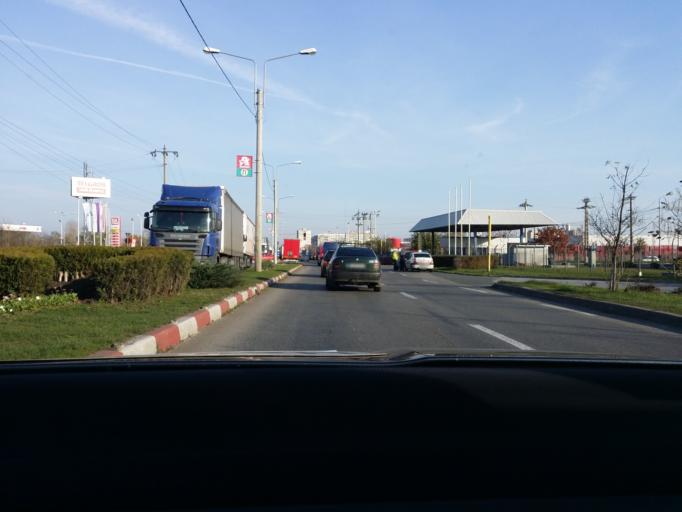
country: RO
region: Prahova
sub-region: Comuna Targsoru Vechi
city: Strejnicu
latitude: 44.9396
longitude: 25.9740
